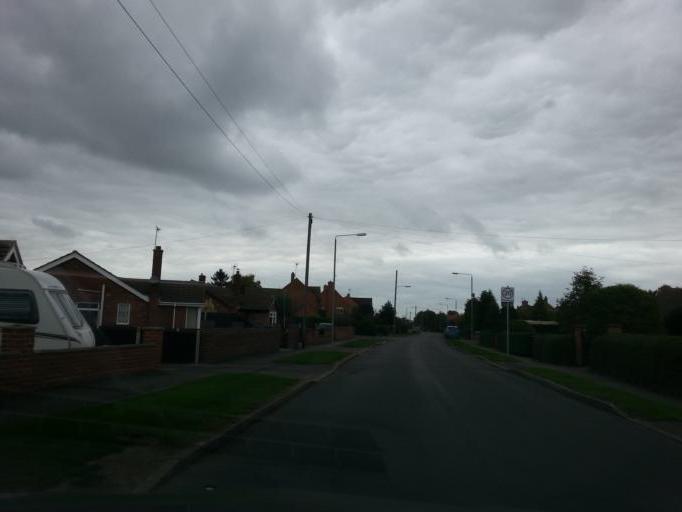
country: GB
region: England
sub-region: Nottinghamshire
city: Newark on Trent
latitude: 53.0578
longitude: -0.7768
